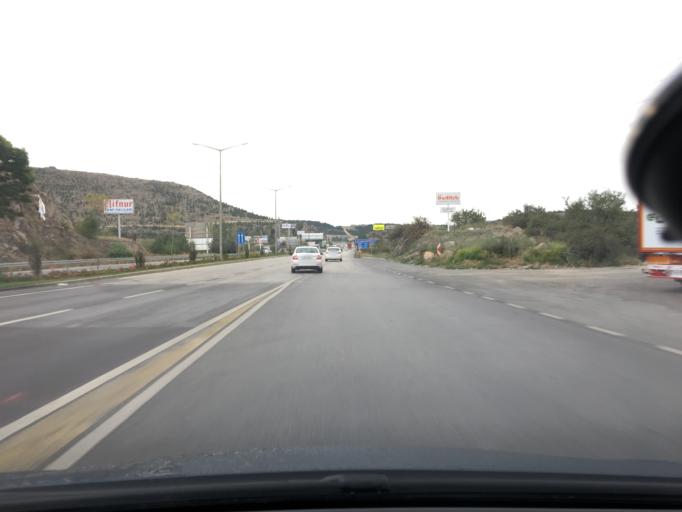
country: TR
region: Afyonkarahisar
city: Afyonkarahisar
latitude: 38.7918
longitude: 30.4523
